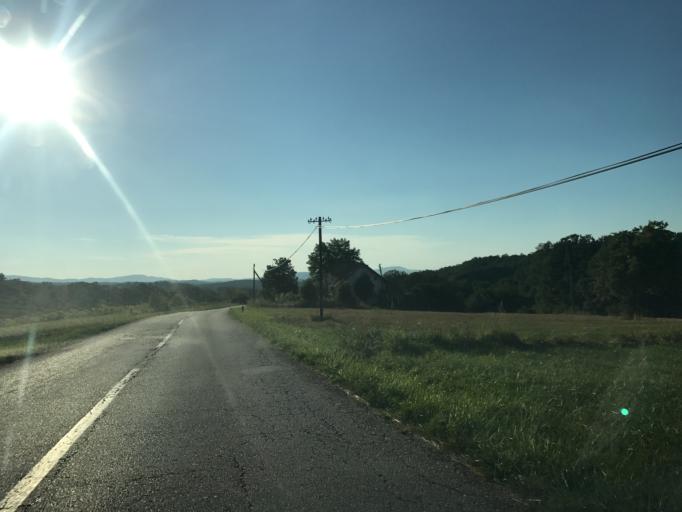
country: RS
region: Central Serbia
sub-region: Borski Okrug
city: Negotin
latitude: 44.2689
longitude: 22.3806
